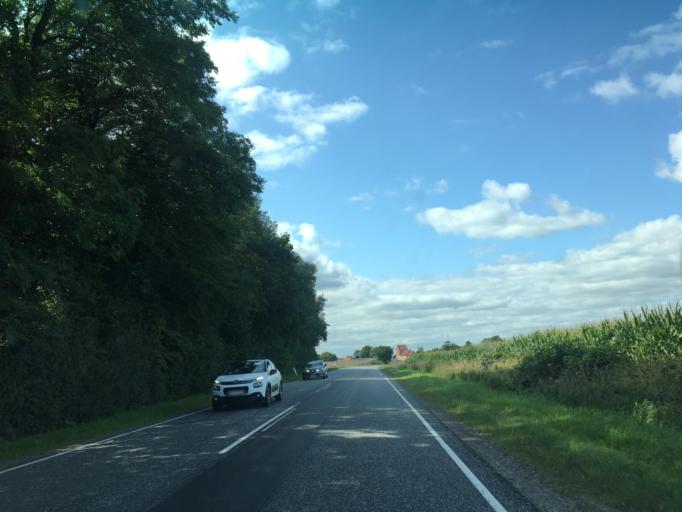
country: DK
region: North Denmark
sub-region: Mariagerfjord Kommune
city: Hobro
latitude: 56.6730
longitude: 9.6846
